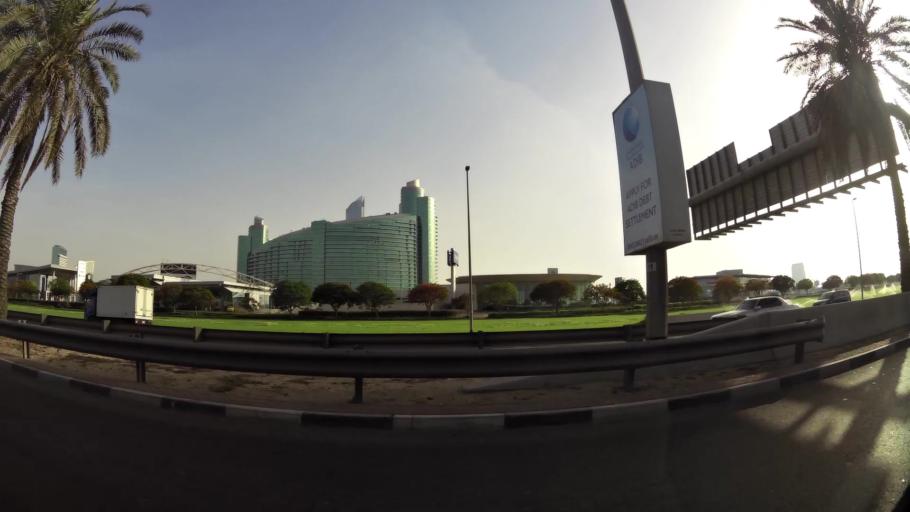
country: AE
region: Ash Shariqah
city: Sharjah
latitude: 25.2350
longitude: 55.3487
